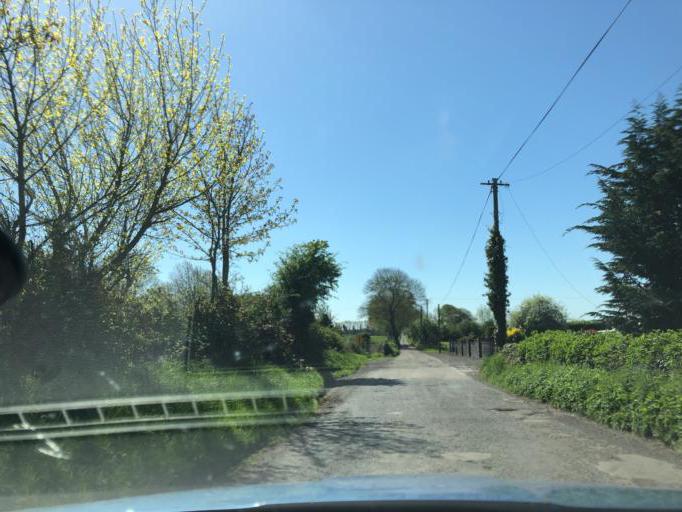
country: IE
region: Connaught
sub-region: County Galway
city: Portumna
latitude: 53.1488
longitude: -8.3395
